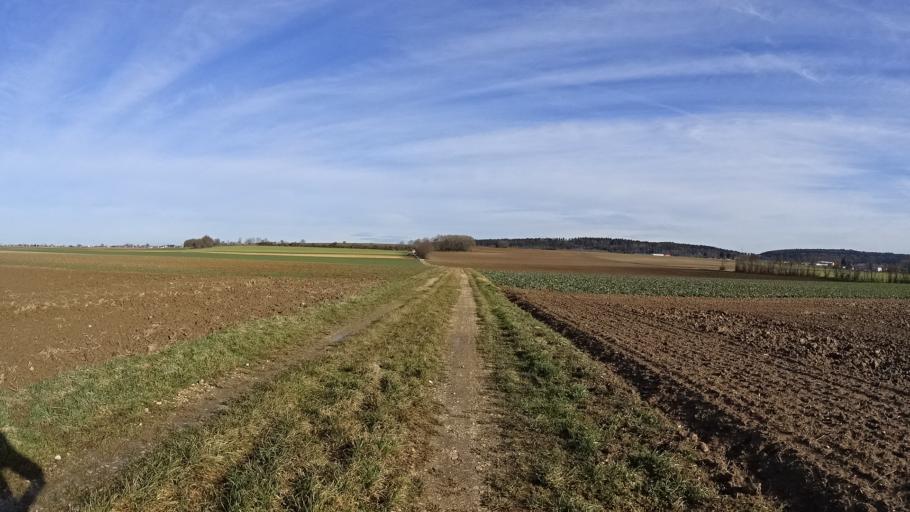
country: DE
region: Bavaria
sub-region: Upper Bavaria
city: Eitensheim
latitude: 48.8300
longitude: 11.3413
